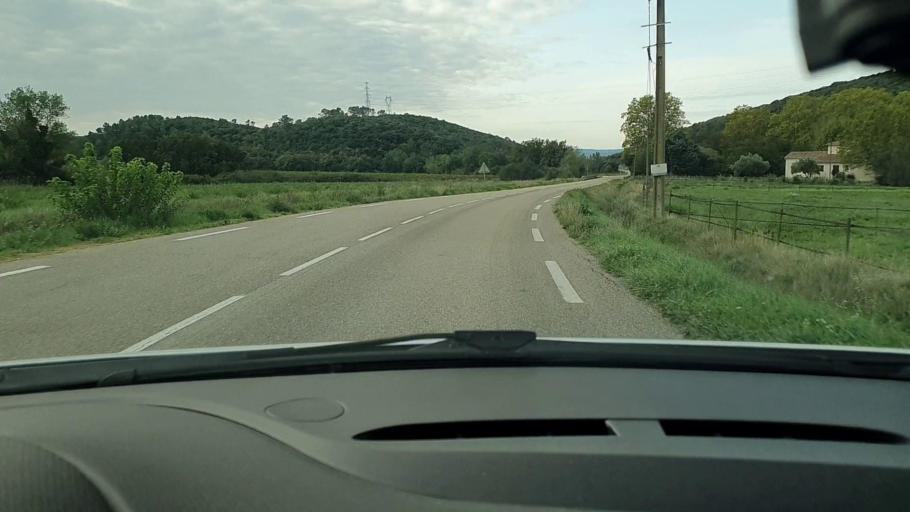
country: FR
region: Languedoc-Roussillon
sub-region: Departement du Gard
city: Mons
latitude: 44.1054
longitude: 4.2268
